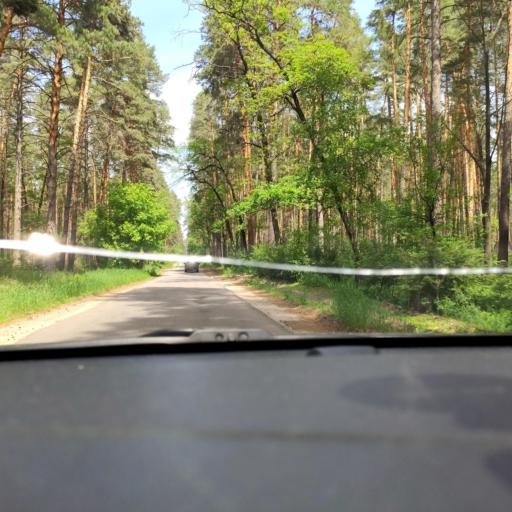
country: RU
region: Voronezj
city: Somovo
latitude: 51.7908
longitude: 39.3108
